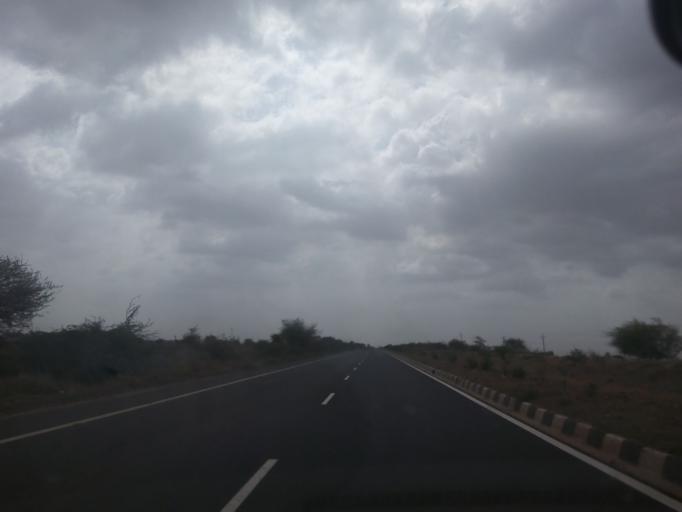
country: IN
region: Gujarat
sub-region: Surendranagar
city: Halvad
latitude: 23.0107
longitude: 71.0480
